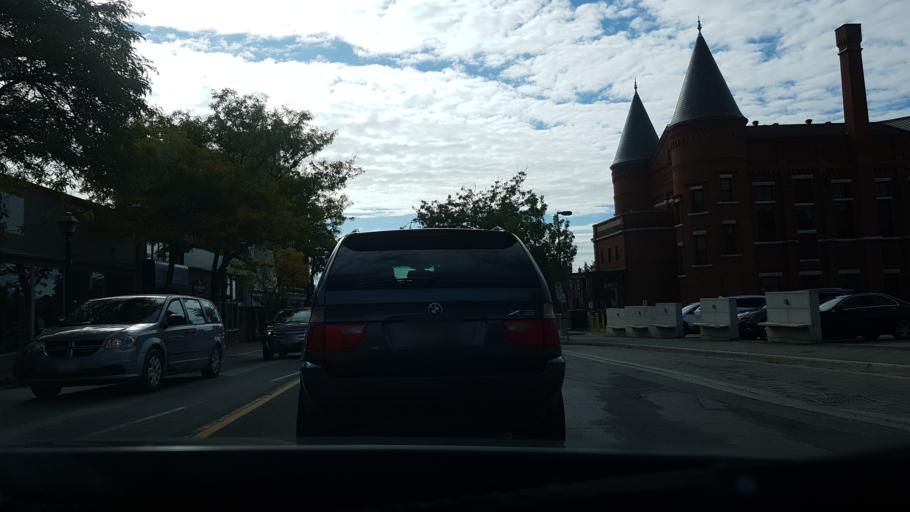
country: CA
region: Ontario
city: Orillia
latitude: 44.6091
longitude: -79.4205
